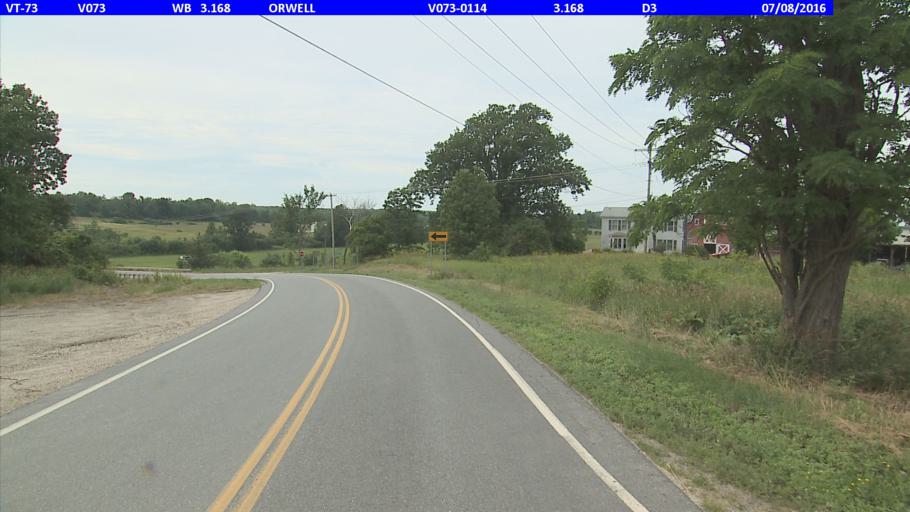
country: US
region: Vermont
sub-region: Rutland County
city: Brandon
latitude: 43.8012
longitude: -73.2442
